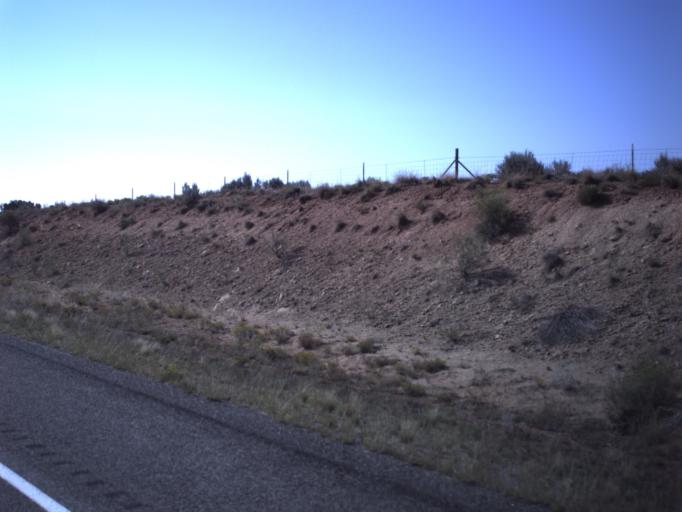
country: US
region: Utah
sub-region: San Juan County
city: Blanding
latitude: 37.4819
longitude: -109.4710
